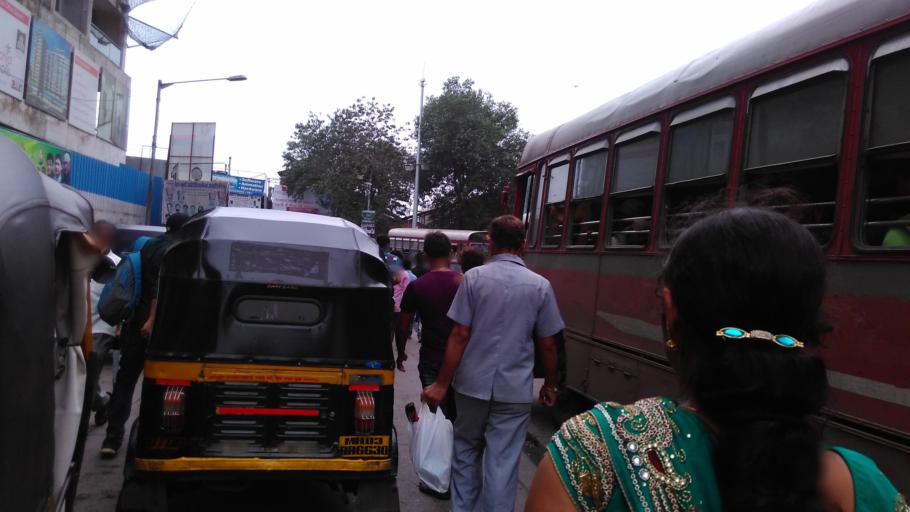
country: IN
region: Maharashtra
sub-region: Mumbai Suburban
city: Mumbai
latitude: 19.0645
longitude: 72.8812
